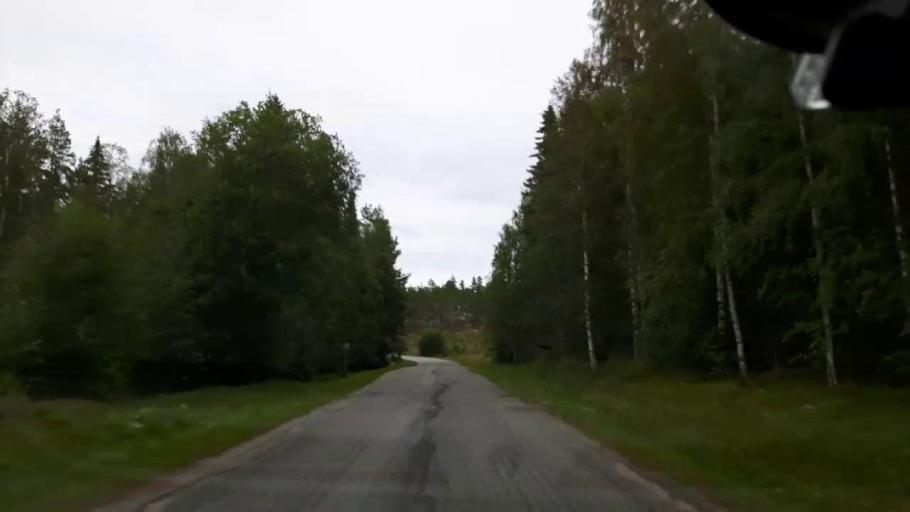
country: SE
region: Vaesternorrland
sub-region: Ange Kommun
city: Fransta
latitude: 62.7721
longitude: 16.0503
